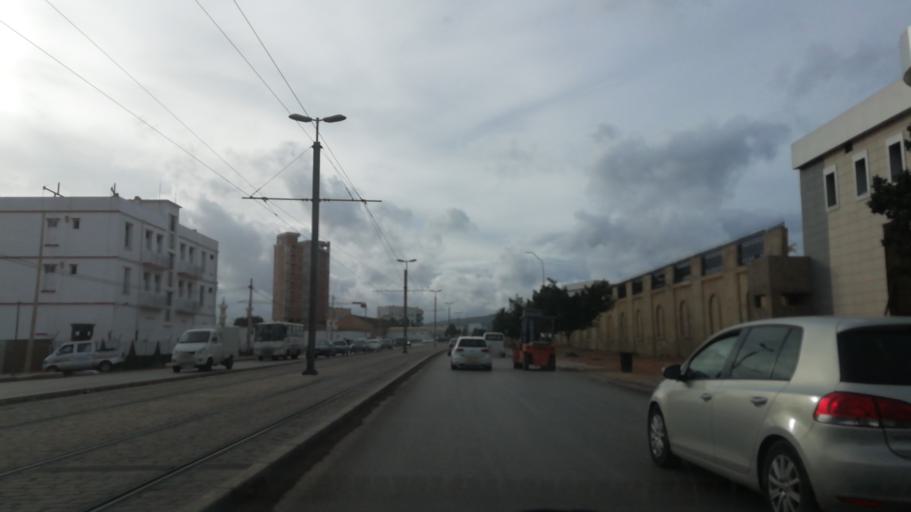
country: DZ
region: Oran
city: Oran
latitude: 35.6968
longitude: -0.6090
